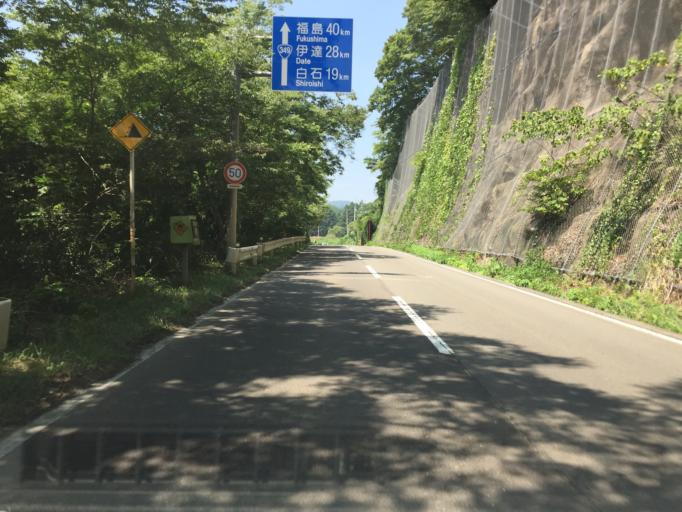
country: JP
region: Miyagi
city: Marumori
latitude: 37.9244
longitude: 140.7601
